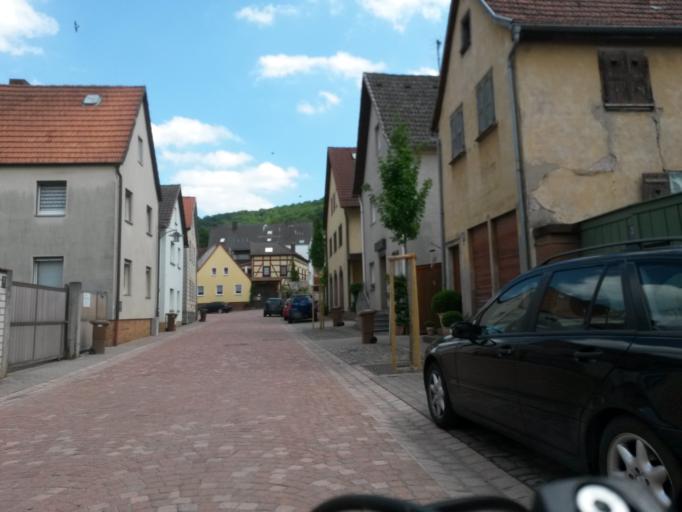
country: DE
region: Bavaria
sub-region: Regierungsbezirk Unterfranken
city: Euerdorf
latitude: 50.1491
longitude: 10.0239
